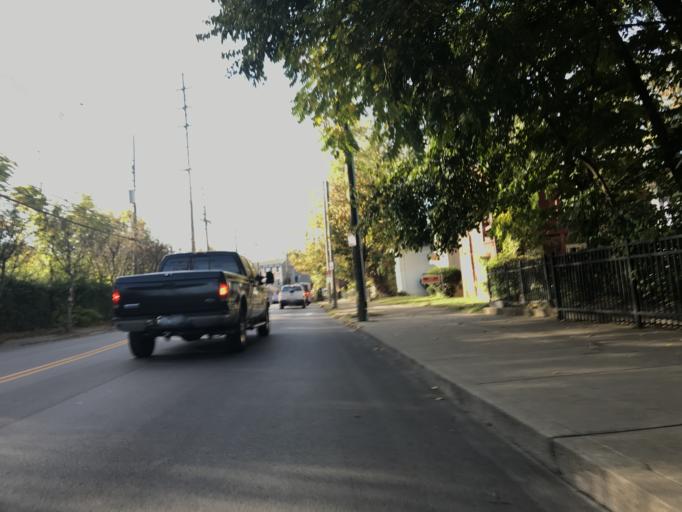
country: US
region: Indiana
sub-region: Clark County
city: Jeffersonville
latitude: 38.2582
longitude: -85.7203
